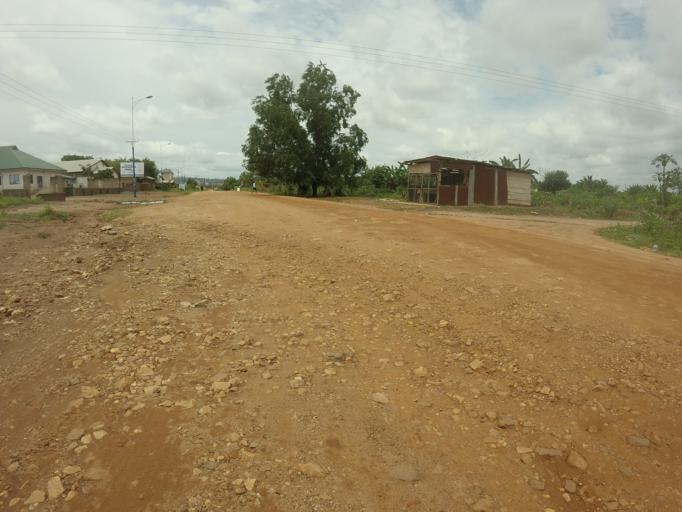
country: GH
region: Volta
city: Ho
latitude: 6.5801
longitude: 0.4634
